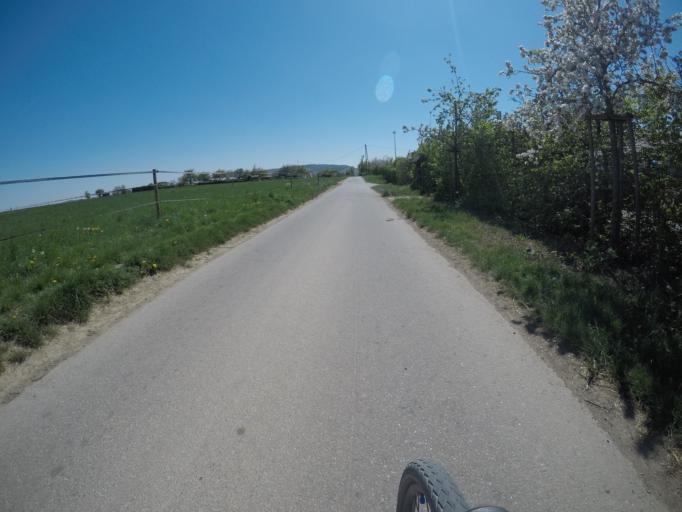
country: DE
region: Baden-Wuerttemberg
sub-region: Regierungsbezirk Stuttgart
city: Fellbach
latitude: 48.8386
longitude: 9.2759
